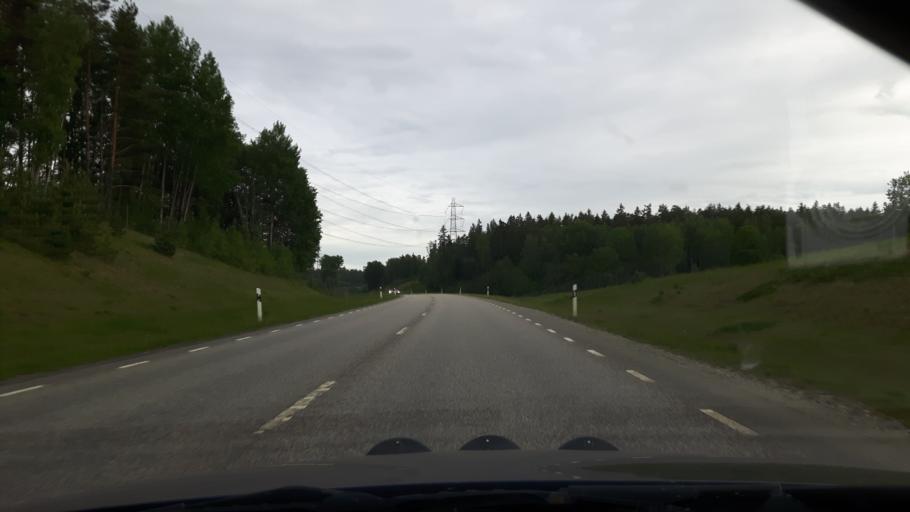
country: SE
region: Stockholm
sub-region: Sodertalje Kommun
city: Pershagen
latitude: 59.1770
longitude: 17.6903
